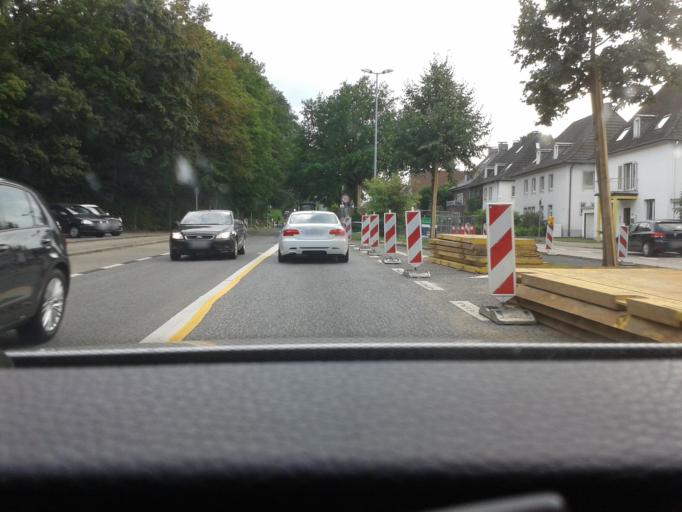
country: DE
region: North Rhine-Westphalia
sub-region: Regierungsbezirk Dusseldorf
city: Duisburg
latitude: 51.4373
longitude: 6.8241
